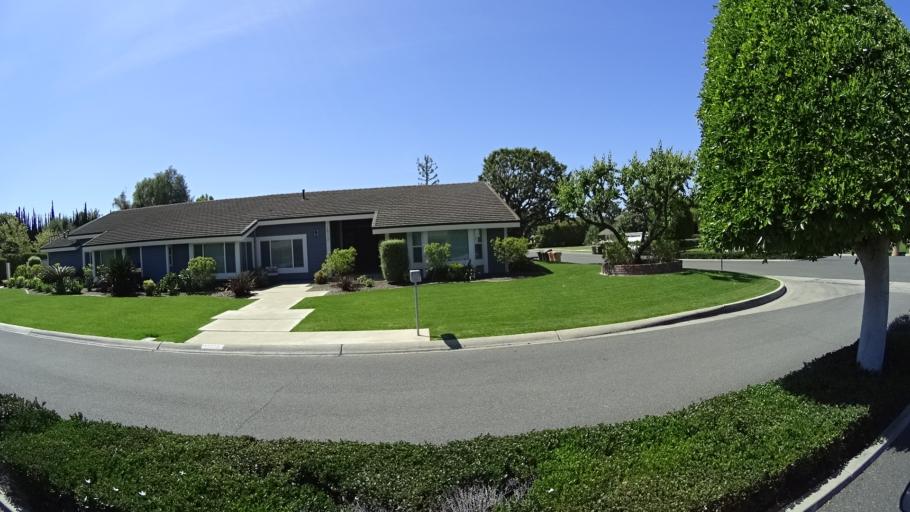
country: US
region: California
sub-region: Orange County
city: Villa Park
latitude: 33.8167
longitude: -117.8050
